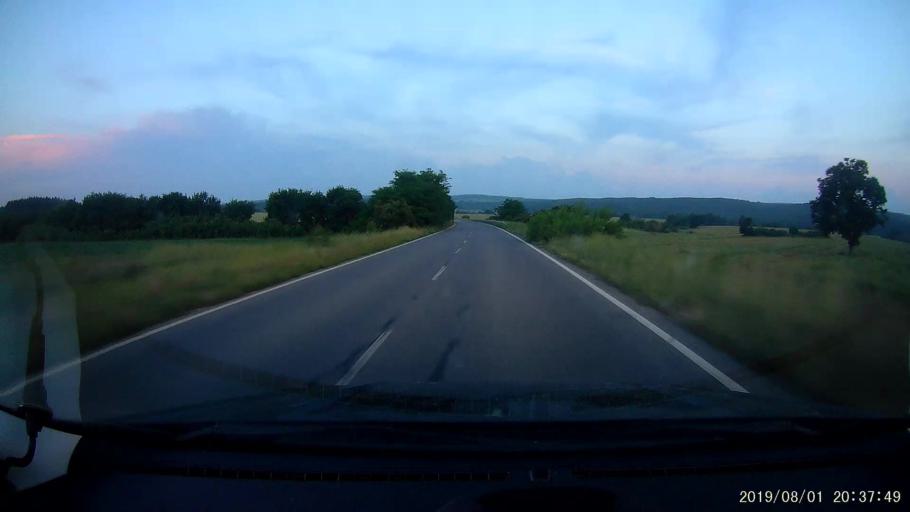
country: BG
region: Yambol
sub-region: Obshtina Elkhovo
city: Elkhovo
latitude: 42.0396
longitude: 26.5959
